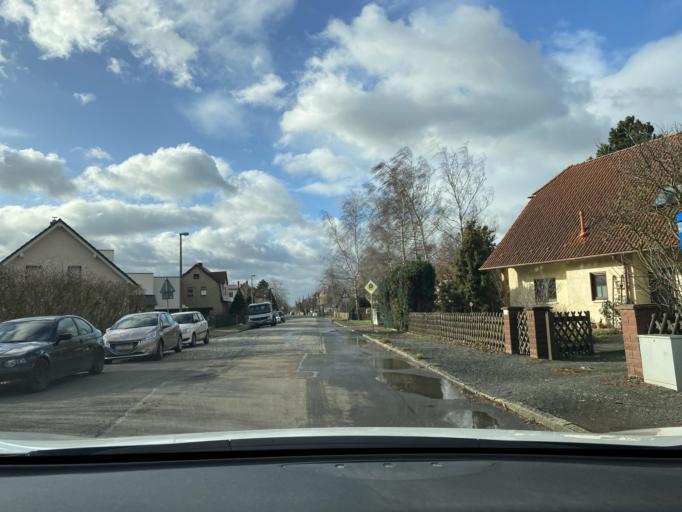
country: DE
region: Saxony
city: Zwenkau
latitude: 51.2629
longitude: 12.3078
